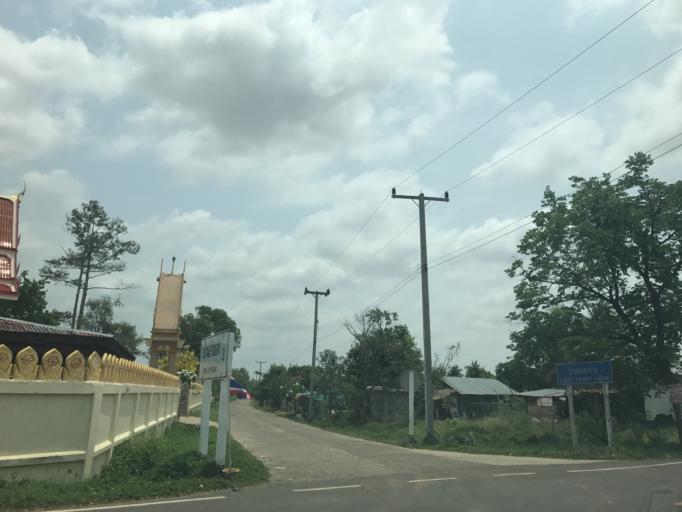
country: TH
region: Surin
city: Chom Phra
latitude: 15.0642
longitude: 103.6637
